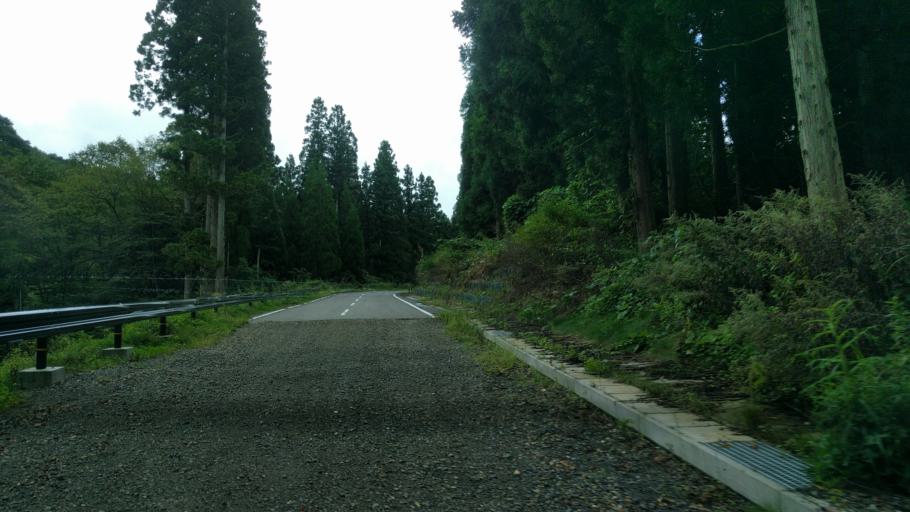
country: JP
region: Fukushima
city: Kitakata
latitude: 37.5211
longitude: 139.7600
